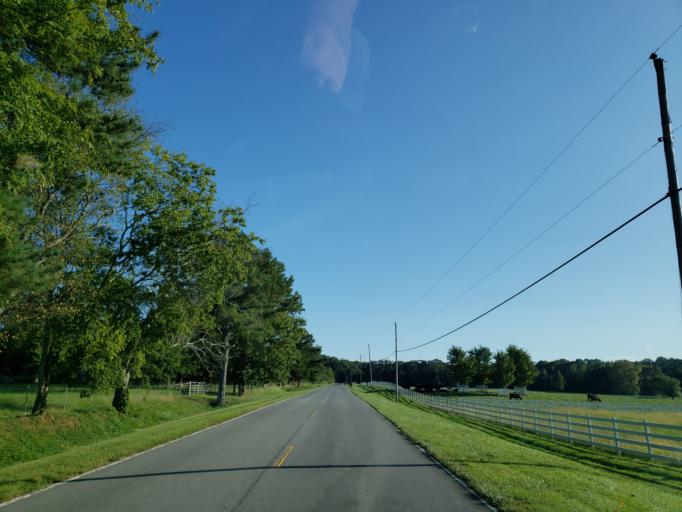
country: US
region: Georgia
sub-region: Bartow County
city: Rydal
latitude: 34.3091
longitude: -84.7741
